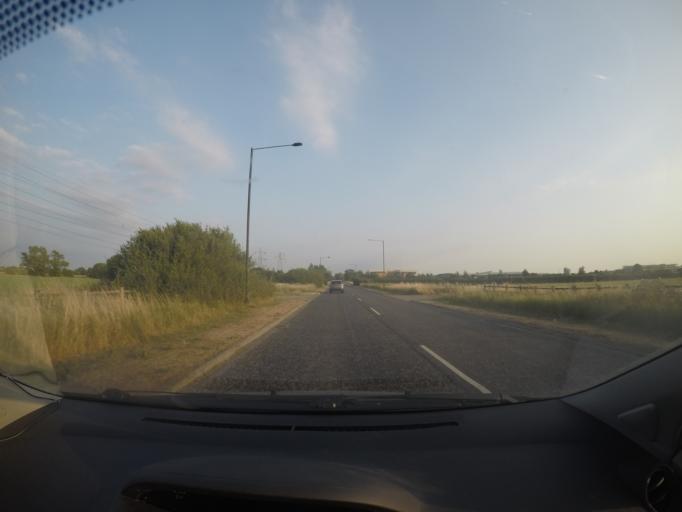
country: GB
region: England
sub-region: City of York
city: Huntington
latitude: 53.9927
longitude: -1.0422
